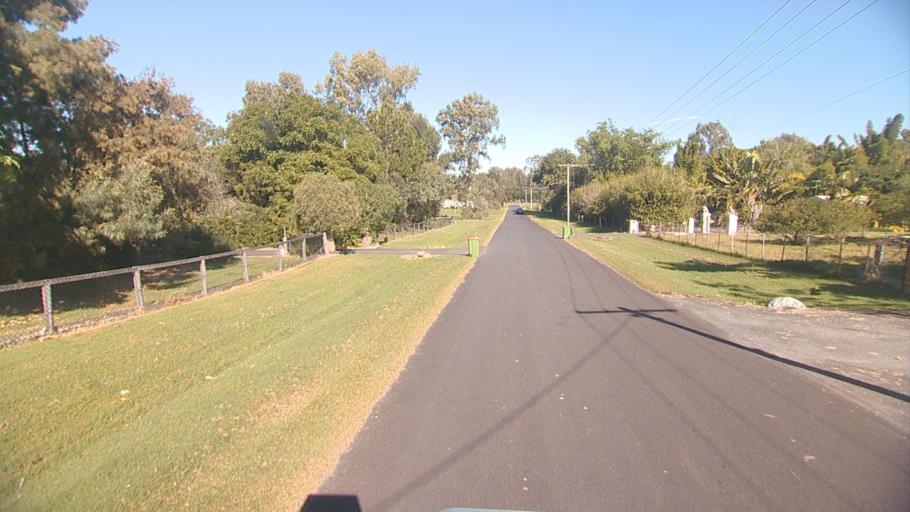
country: AU
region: Queensland
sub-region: Logan
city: Park Ridge South
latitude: -27.7236
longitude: 153.0340
